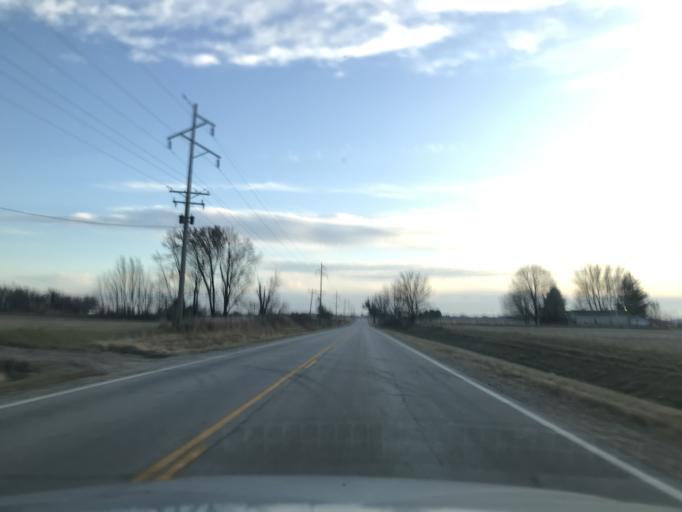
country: US
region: Illinois
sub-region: Warren County
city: Monmouth
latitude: 41.0331
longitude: -90.7461
